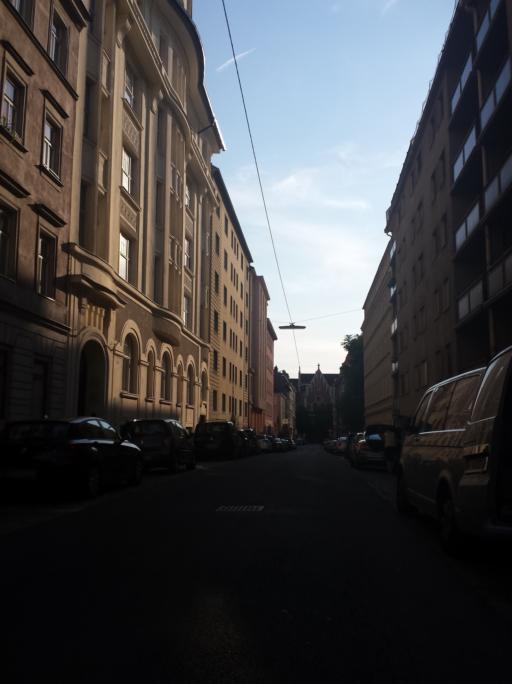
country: AT
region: Vienna
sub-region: Wien Stadt
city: Vienna
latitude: 48.1911
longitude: 16.3791
